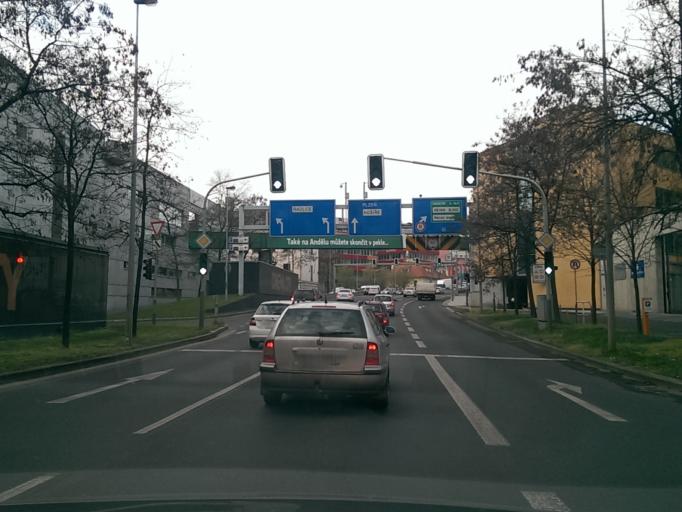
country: CZ
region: Praha
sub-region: Praha 1
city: Mala Strana
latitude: 50.0738
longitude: 14.4019
